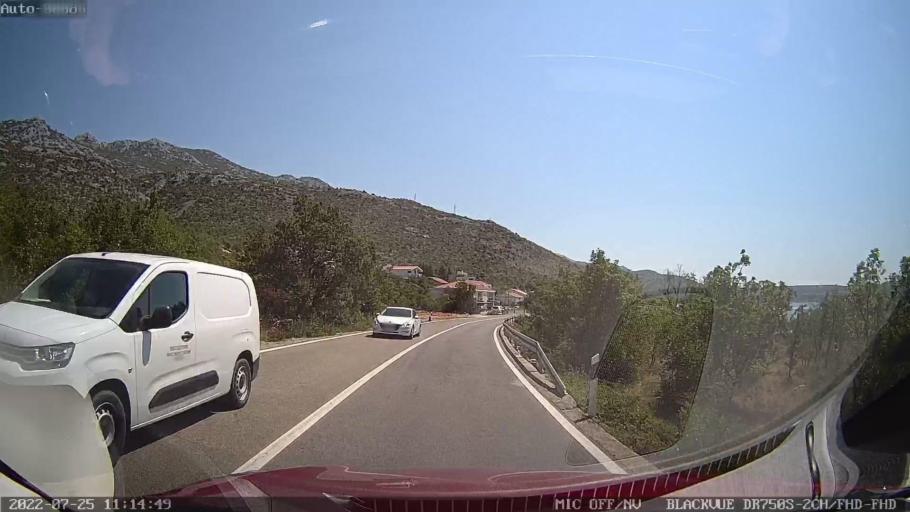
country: HR
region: Zadarska
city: Posedarje
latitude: 44.2736
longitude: 15.5028
